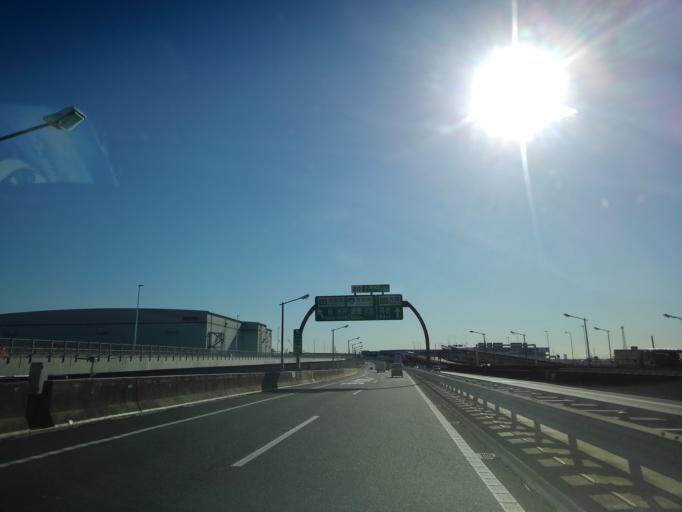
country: JP
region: Saitama
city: Yashio-shi
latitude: 35.8405
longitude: 139.8549
